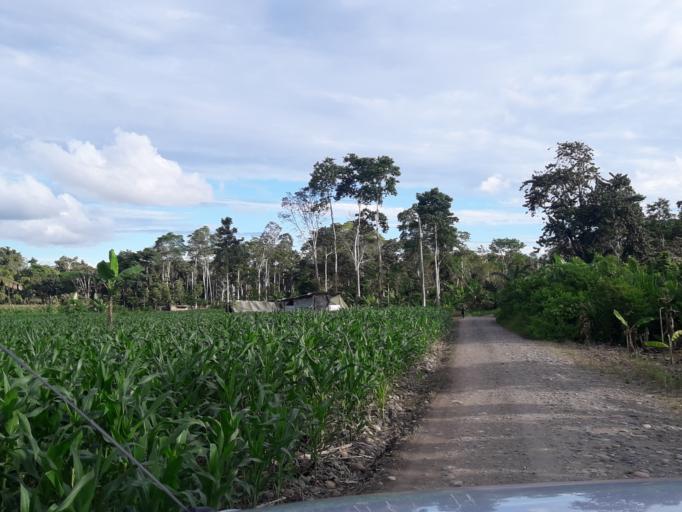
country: EC
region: Orellana
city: Boca Suno
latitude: -0.8943
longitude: -77.3079
